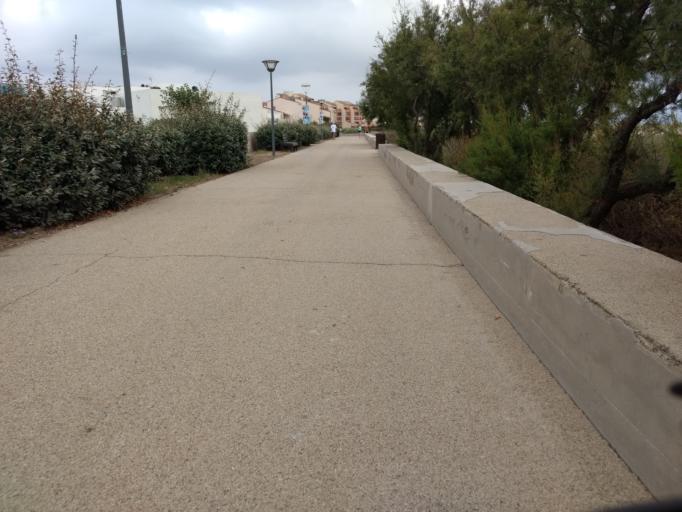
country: FR
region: Languedoc-Roussillon
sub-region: Departement des Pyrenees-Orientales
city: Le Barcares
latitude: 42.8485
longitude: 3.0433
